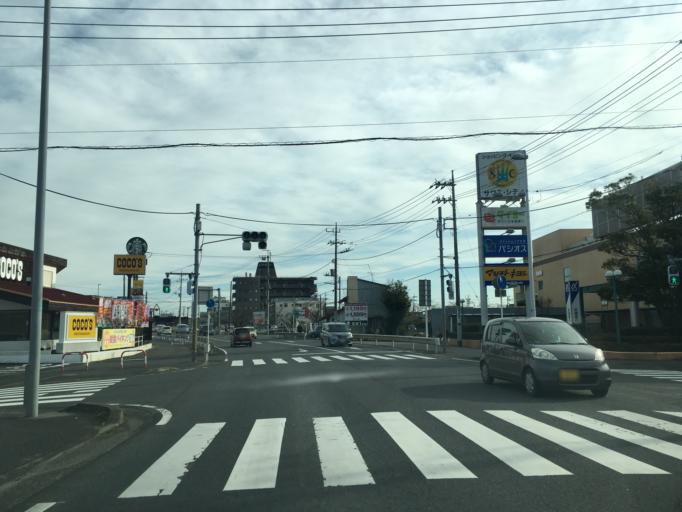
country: JP
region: Chiba
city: Katori-shi
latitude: 35.9011
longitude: 140.4892
